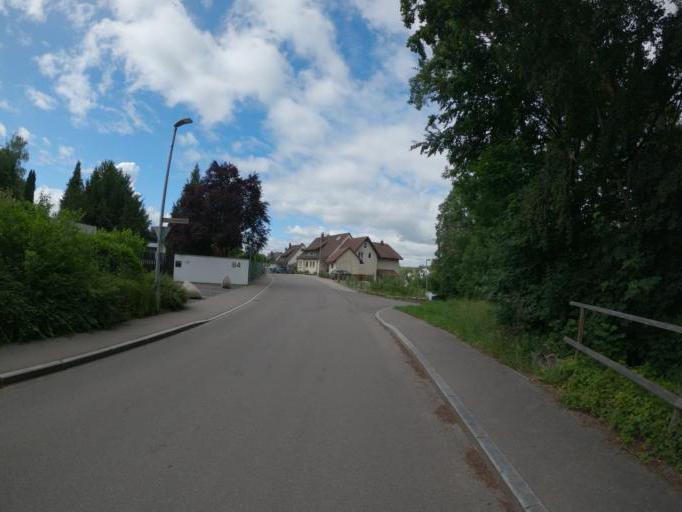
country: DE
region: Baden-Wuerttemberg
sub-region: Regierungsbezirk Stuttgart
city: Ebersbach an der Fils
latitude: 48.7228
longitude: 9.5223
